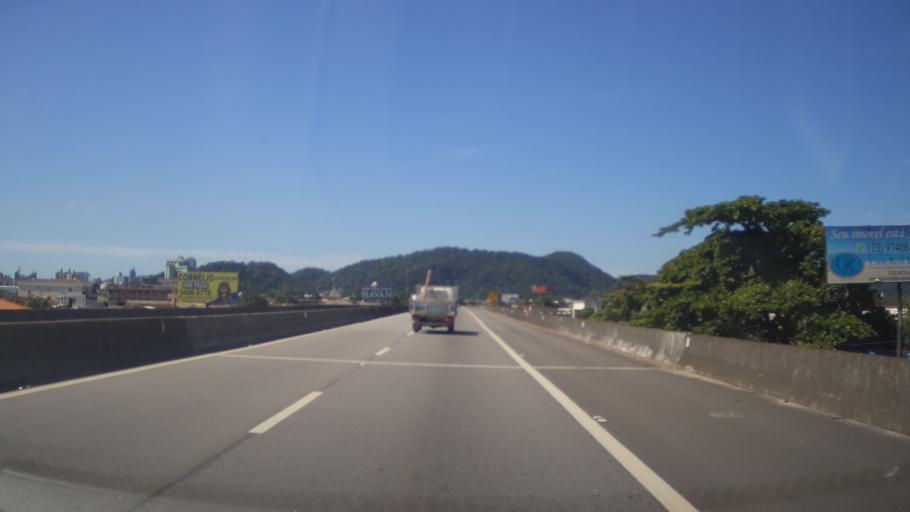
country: BR
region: Sao Paulo
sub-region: Sao Vicente
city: Sao Vicente
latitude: -23.9620
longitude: -46.4037
